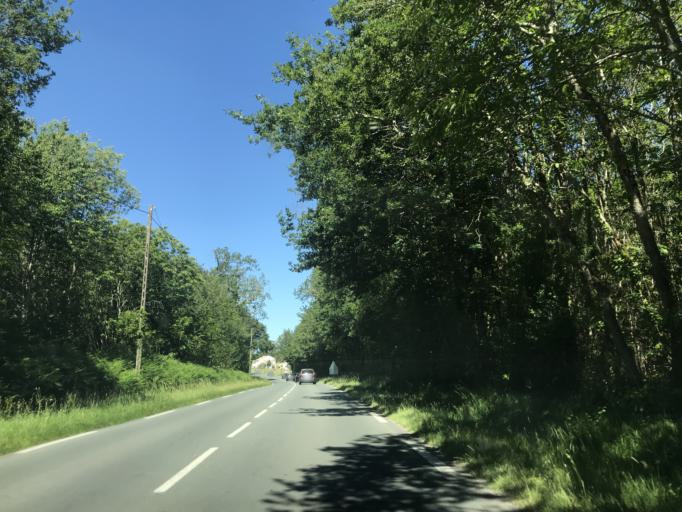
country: FR
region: Poitou-Charentes
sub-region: Departement de la Charente-Maritime
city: Cozes
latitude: 45.5781
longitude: -0.7836
